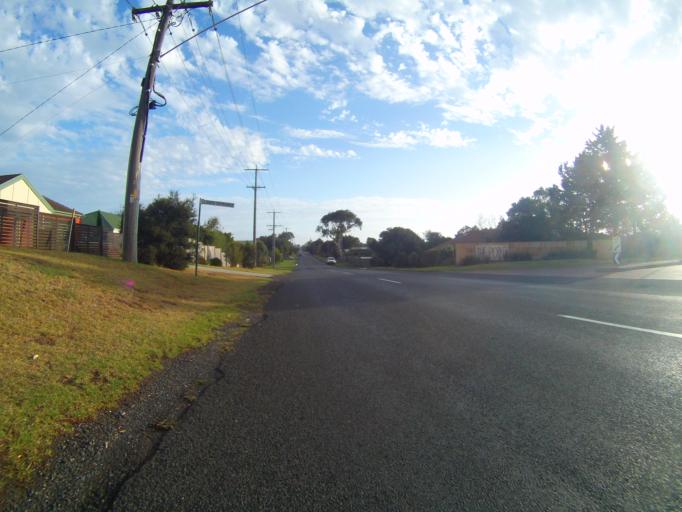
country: AU
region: Victoria
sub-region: Queenscliffe
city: Queenscliff
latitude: -38.2689
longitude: 144.6167
